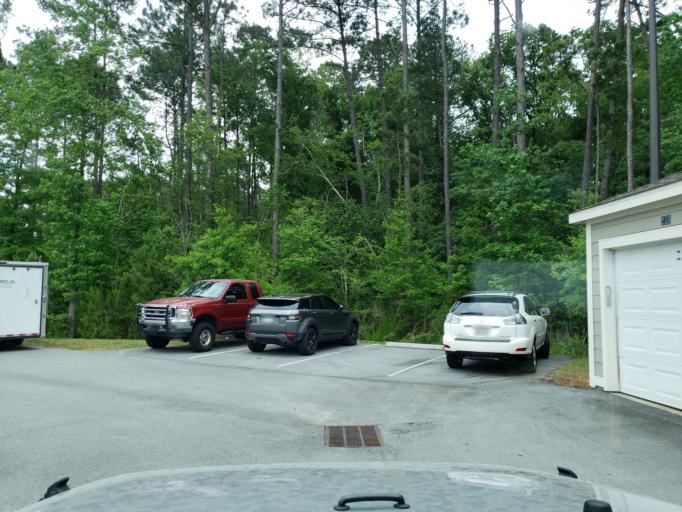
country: US
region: Georgia
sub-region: Chatham County
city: Pooler
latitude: 32.1736
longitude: -81.2287
